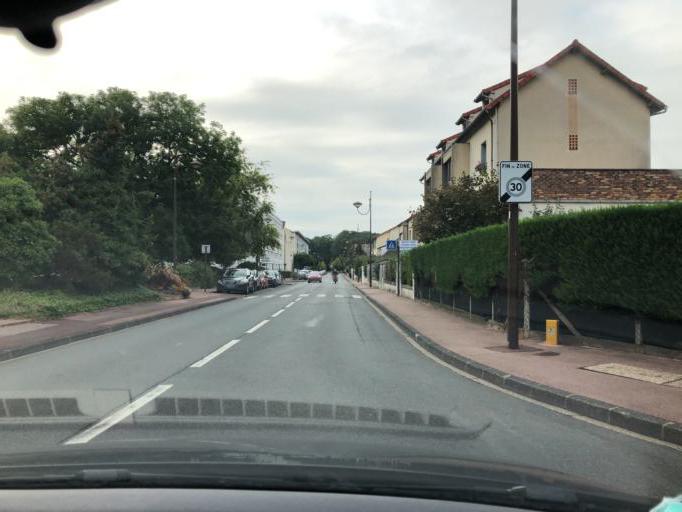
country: FR
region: Ile-de-France
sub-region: Departement des Yvelines
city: Velizy-Villacoublay
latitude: 48.7851
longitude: 2.1897
